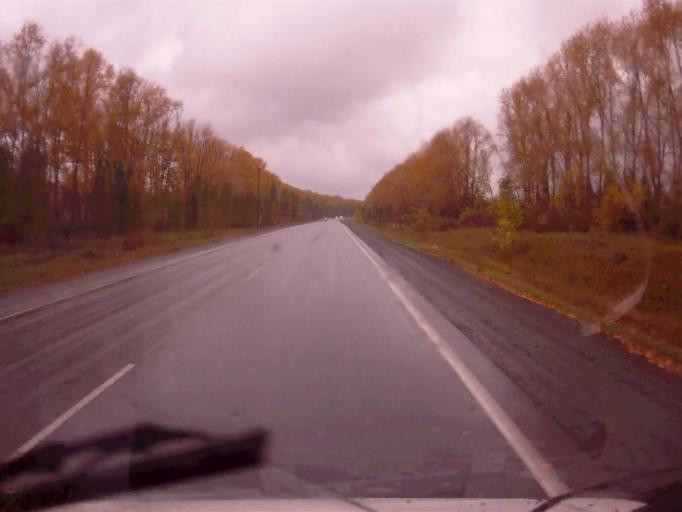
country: RU
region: Chelyabinsk
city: Argayash
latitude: 55.4486
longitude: 60.9428
